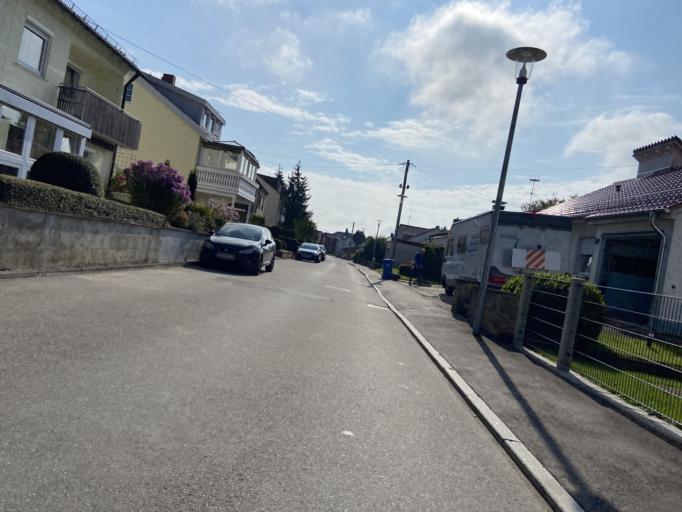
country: DE
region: Baden-Wuerttemberg
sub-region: Tuebingen Region
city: Inzigkofen
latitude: 48.0918
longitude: 9.1941
